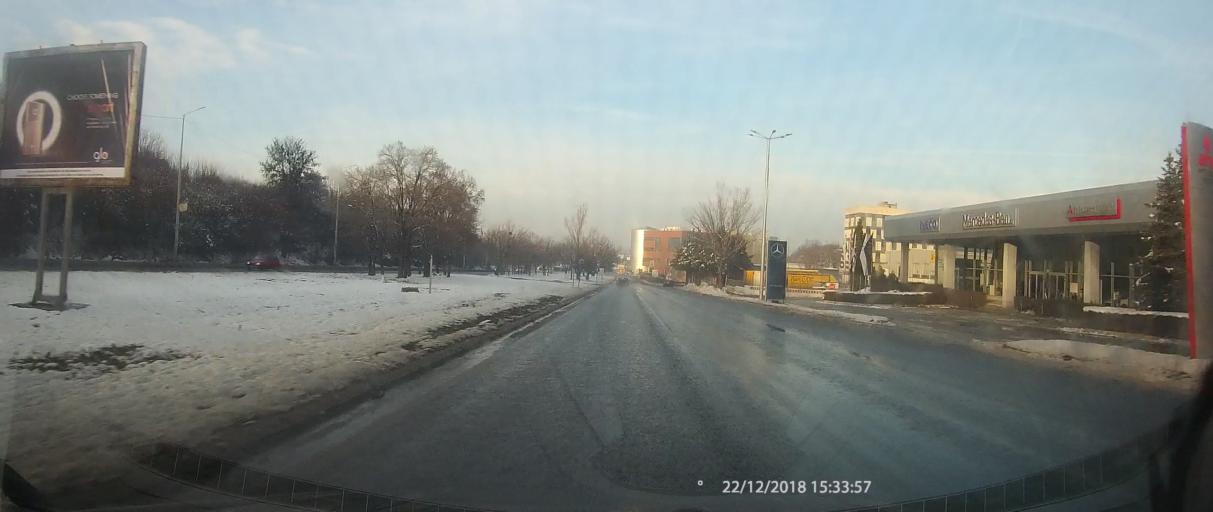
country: BG
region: Ruse
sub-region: Obshtina Ruse
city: Ruse
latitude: 43.8705
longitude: 26.0160
